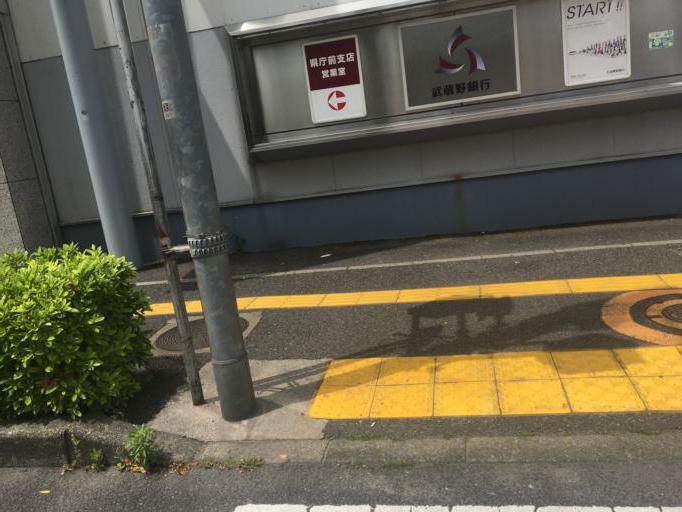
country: JP
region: Saitama
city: Yono
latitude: 35.8578
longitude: 139.6472
